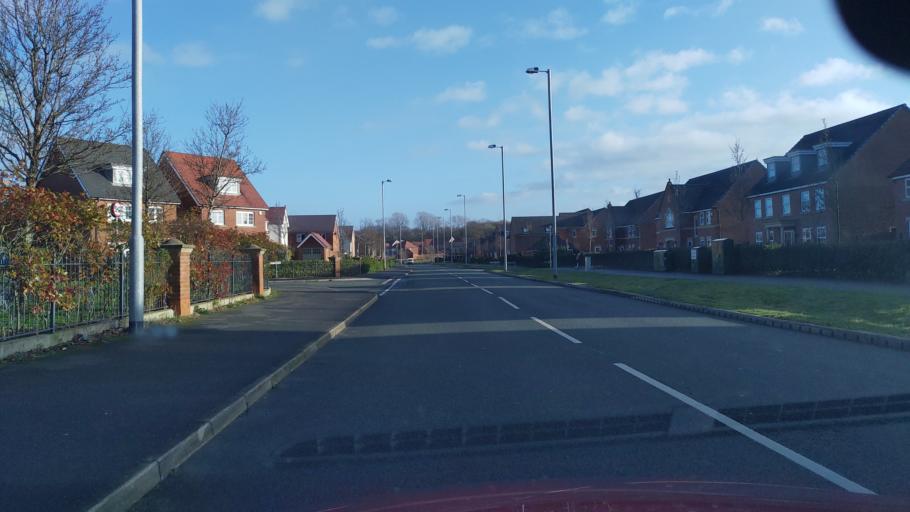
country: GB
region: England
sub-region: Lancashire
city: Clayton-le-Woods
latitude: 53.6797
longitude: -2.6565
